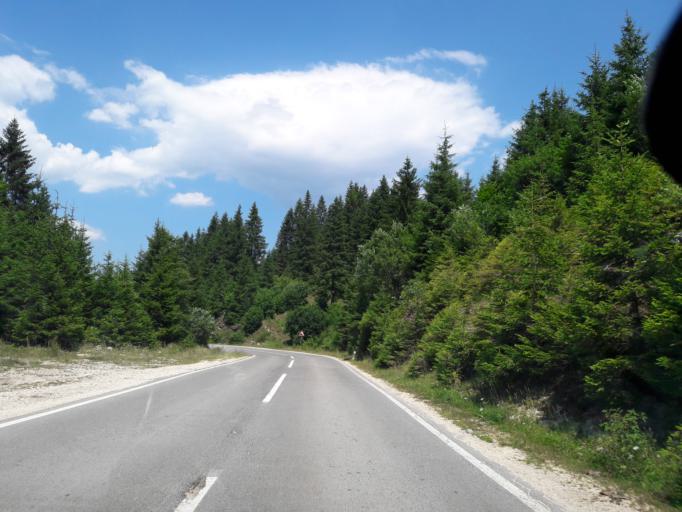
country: BA
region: Republika Srpska
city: Sipovo
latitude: 44.1254
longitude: 17.1826
